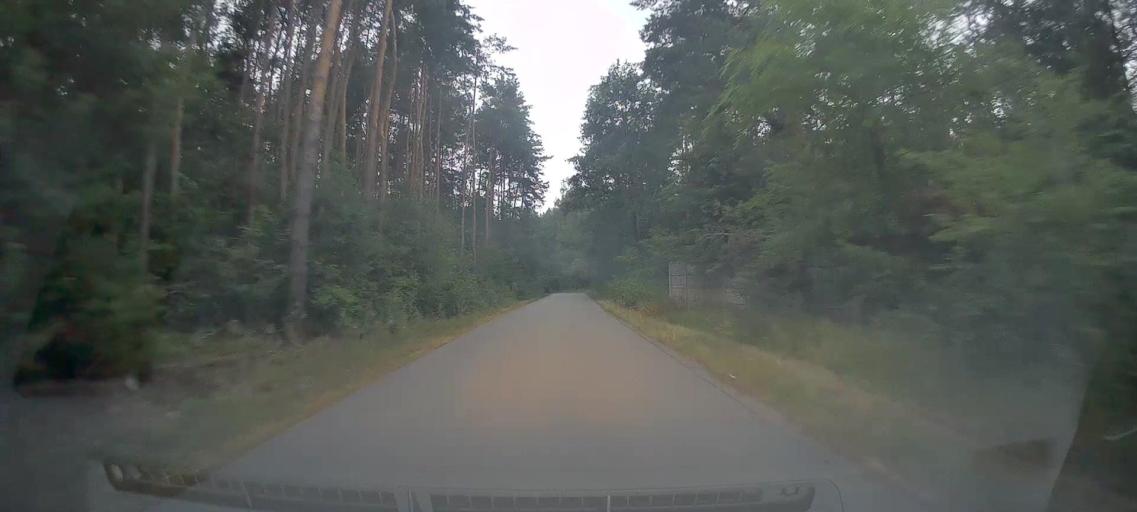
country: PL
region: Masovian Voivodeship
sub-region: Powiat radomski
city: Jedlinsk
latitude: 51.4616
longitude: 21.1066
